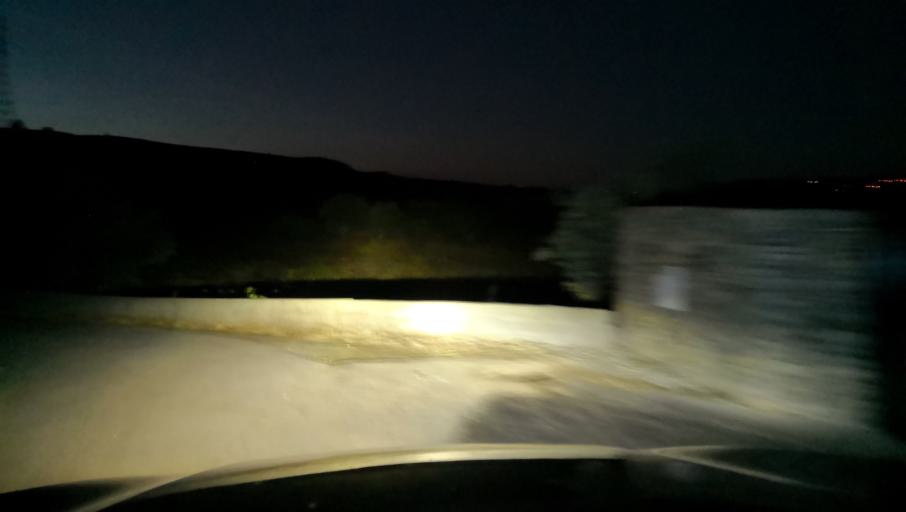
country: PT
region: Viseu
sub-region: Armamar
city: Armamar
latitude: 41.1610
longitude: -7.6957
